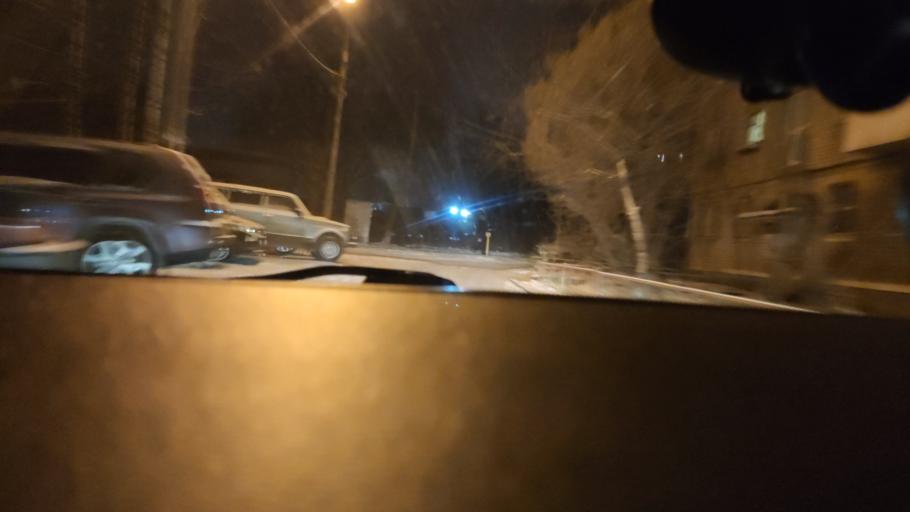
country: RU
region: Perm
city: Perm
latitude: 57.9887
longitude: 56.2720
